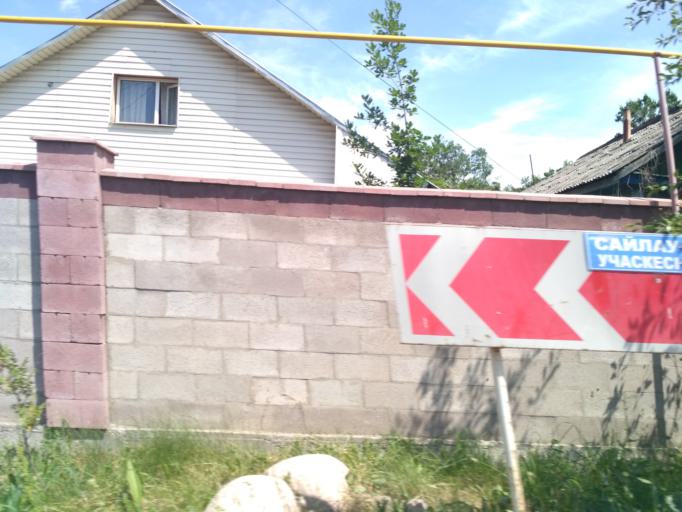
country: KZ
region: Almaty Oblysy
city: Burunday
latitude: 43.1903
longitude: 76.6206
